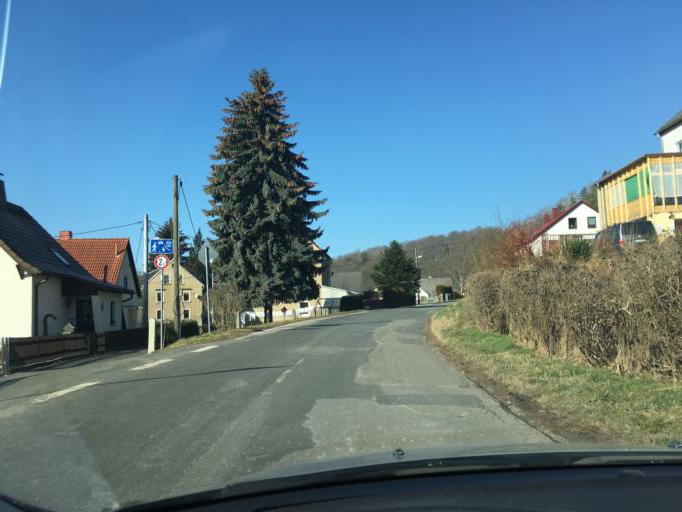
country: DE
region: Saxony
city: Lunzenau
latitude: 50.9667
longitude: 12.7260
